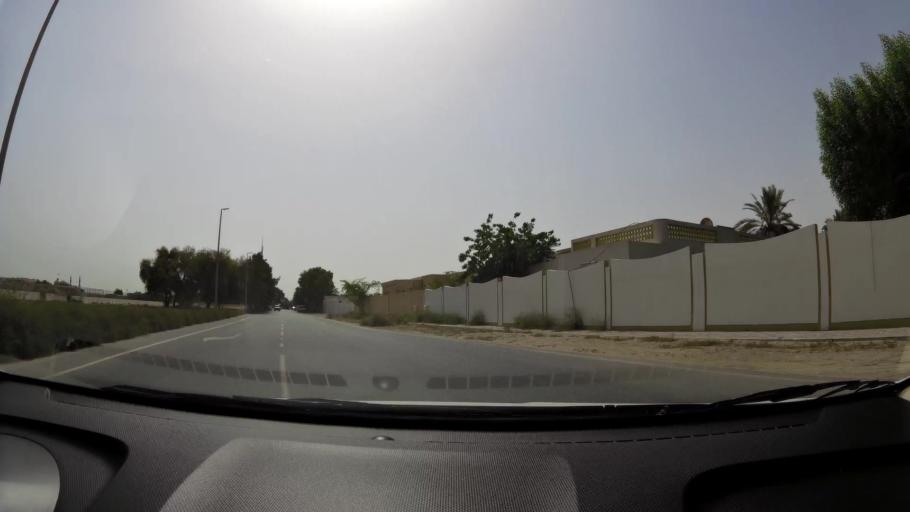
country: AE
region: Ash Shariqah
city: Sharjah
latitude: 25.3520
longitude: 55.4205
